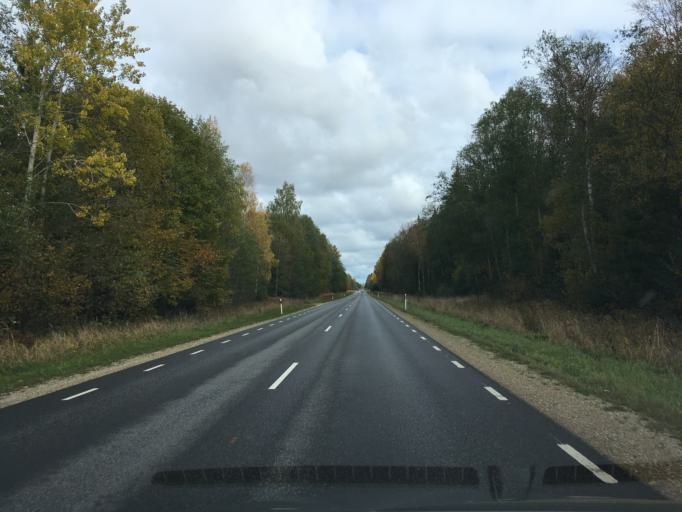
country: EE
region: Harju
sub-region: Anija vald
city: Kehra
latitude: 59.2299
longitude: 25.2792
